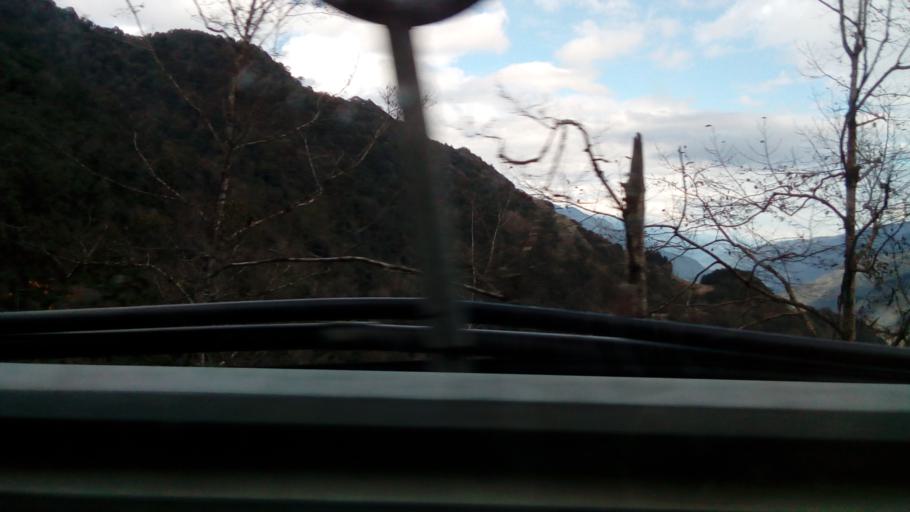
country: TW
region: Taiwan
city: Daxi
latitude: 24.4068
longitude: 121.3598
